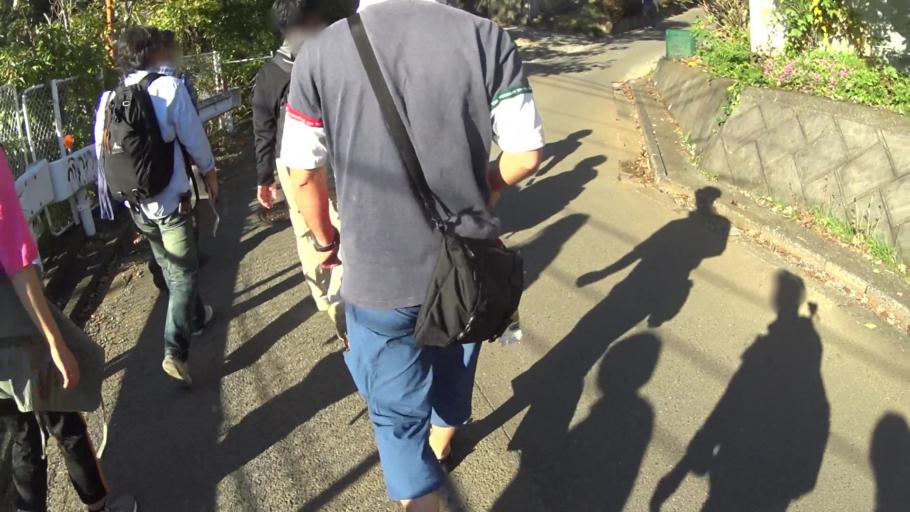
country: JP
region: Tokyo
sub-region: Machida-shi
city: Machida
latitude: 35.5774
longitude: 139.4395
